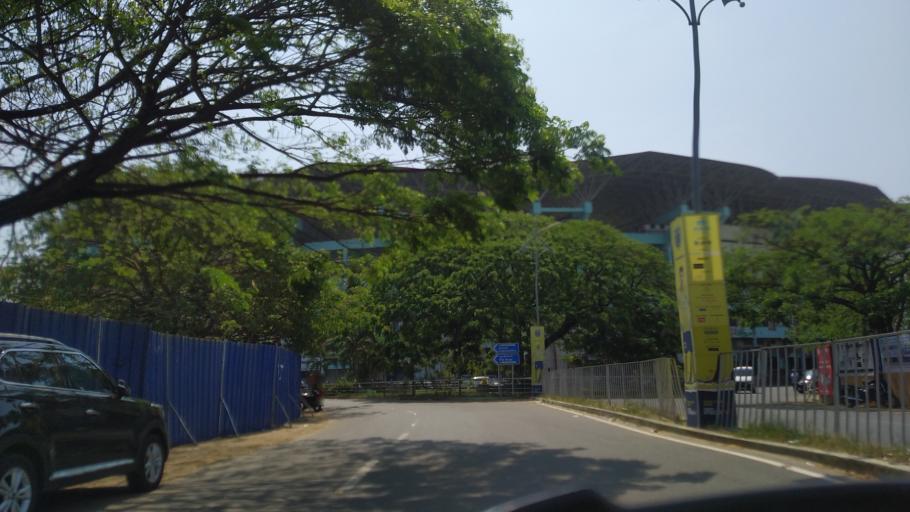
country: IN
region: Kerala
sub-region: Ernakulam
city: Elur
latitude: 9.9991
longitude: 76.3003
